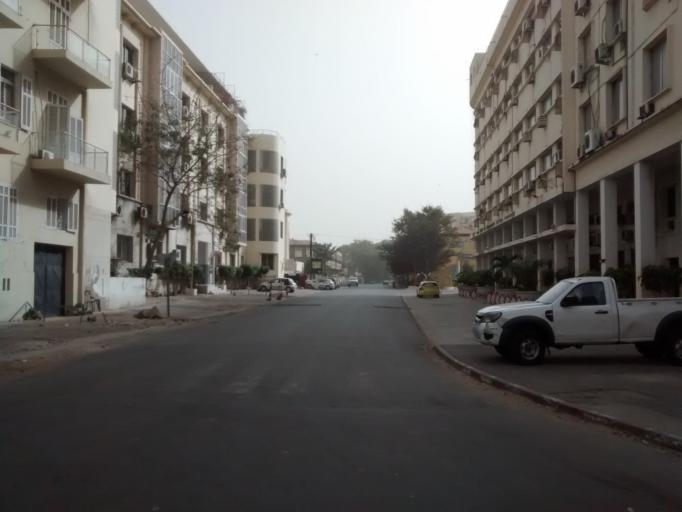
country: SN
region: Dakar
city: Dakar
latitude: 14.6660
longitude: -17.4387
